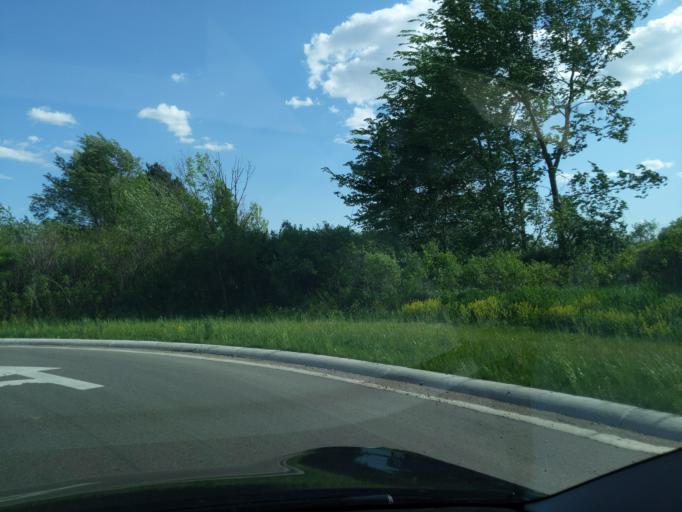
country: US
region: Michigan
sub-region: Eaton County
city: Grand Ledge
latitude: 42.7437
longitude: -84.7595
